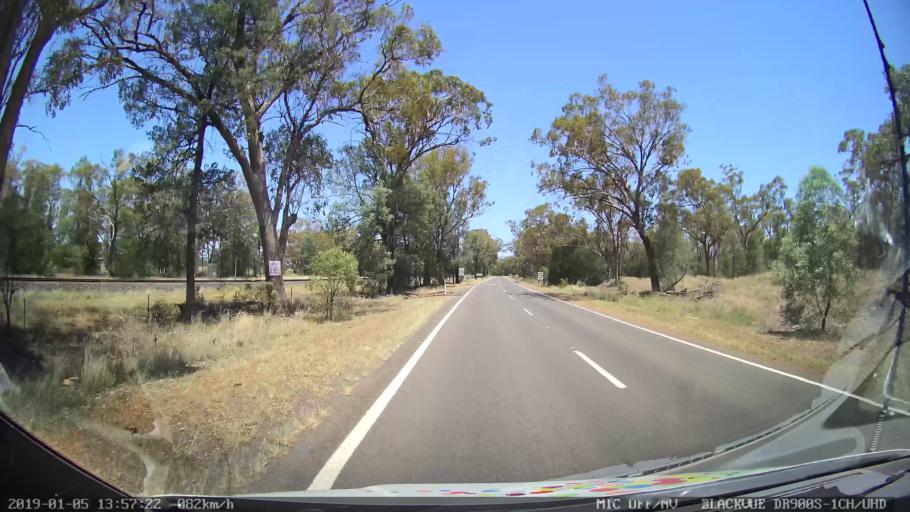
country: AU
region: New South Wales
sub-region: Gunnedah
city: Gunnedah
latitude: -31.1266
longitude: 150.2742
